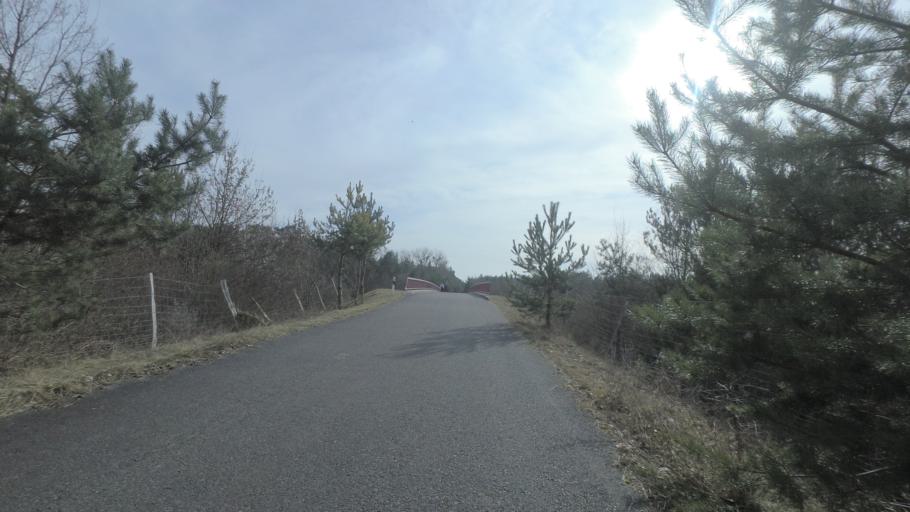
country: DE
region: Brandenburg
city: Ludwigsfelde
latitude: 52.3019
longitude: 13.2292
